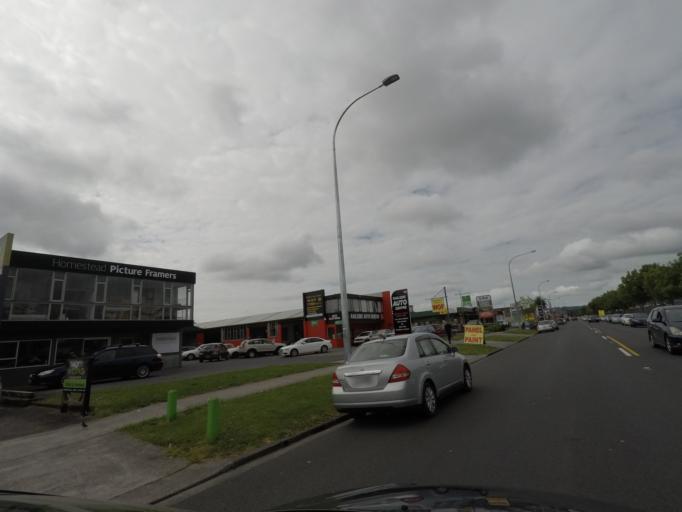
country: NZ
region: Auckland
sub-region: Auckland
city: Rosebank
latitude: -36.8863
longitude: 174.6316
